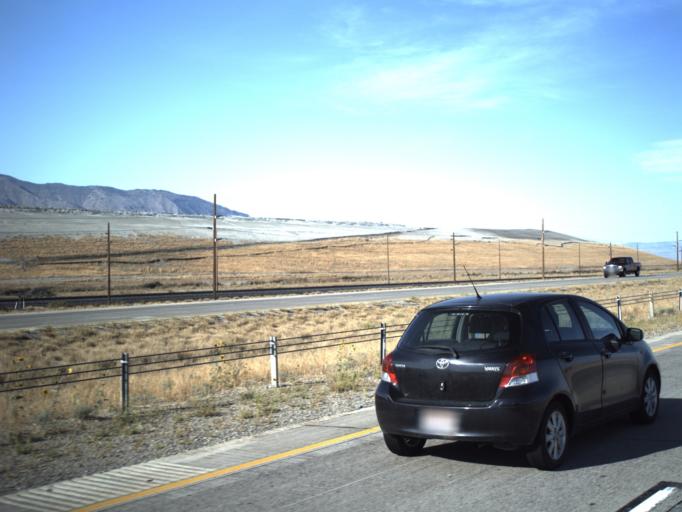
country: US
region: Utah
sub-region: Salt Lake County
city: Magna
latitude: 40.7710
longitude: -112.1370
